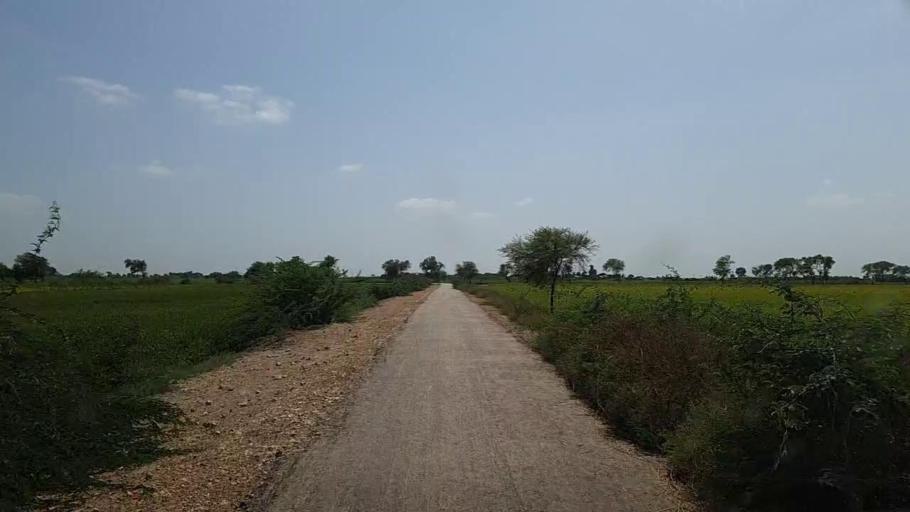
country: PK
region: Sindh
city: Kario
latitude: 24.6452
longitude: 68.5640
